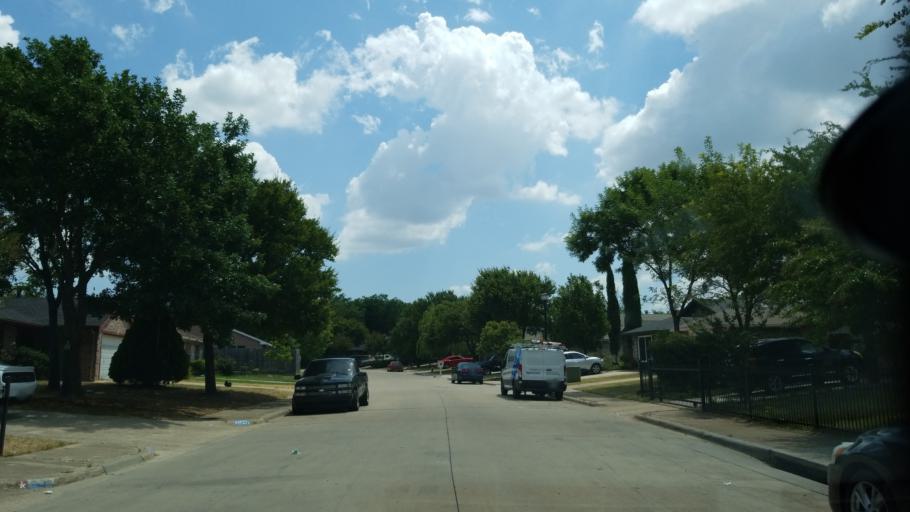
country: US
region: Texas
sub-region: Dallas County
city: Cockrell Hill
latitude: 32.7287
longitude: -96.8940
